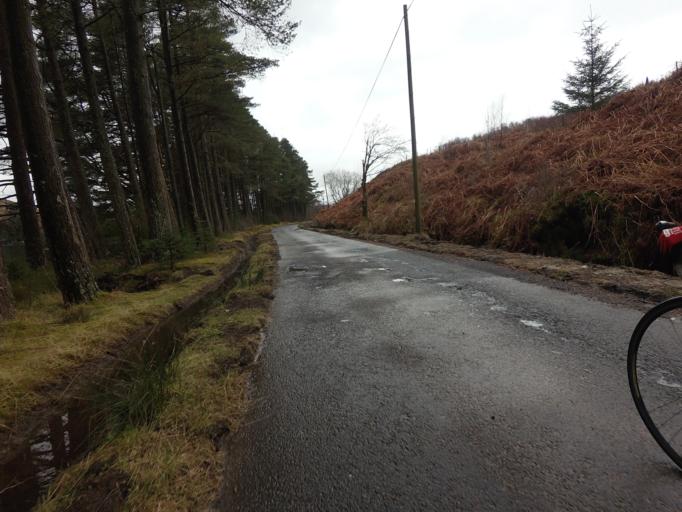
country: GB
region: Scotland
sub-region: Argyll and Bute
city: Garelochhead
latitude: 56.2500
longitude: -4.6494
